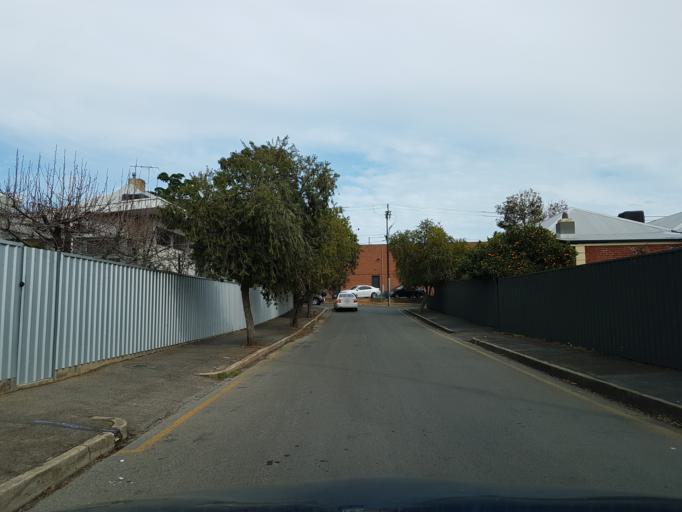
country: AU
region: South Australia
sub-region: Norwood Payneham St Peters
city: Royston Park
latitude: -34.9096
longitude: 138.6299
